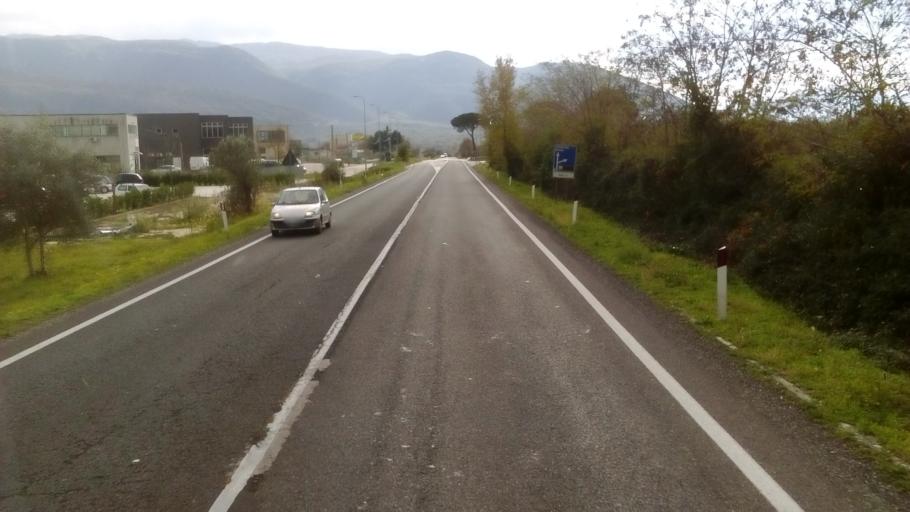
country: IT
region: Molise
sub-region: Provincia di Isernia
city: Macchia d'Isernia
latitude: 41.5427
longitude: 14.1586
